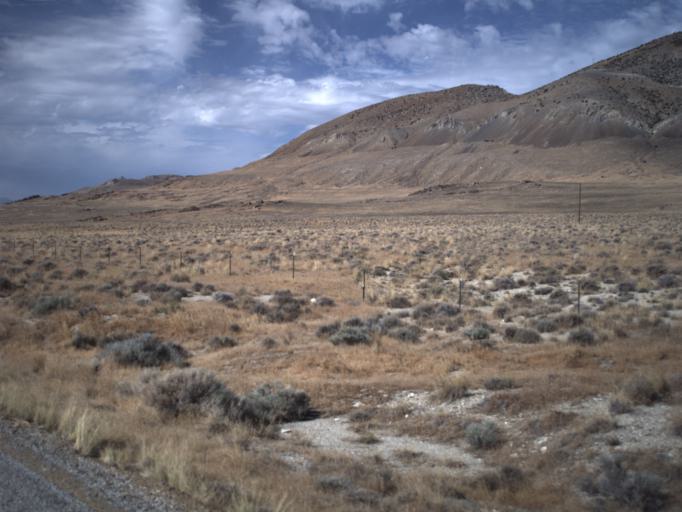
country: US
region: Utah
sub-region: Tooele County
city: Wendover
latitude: 41.4750
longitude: -113.6360
